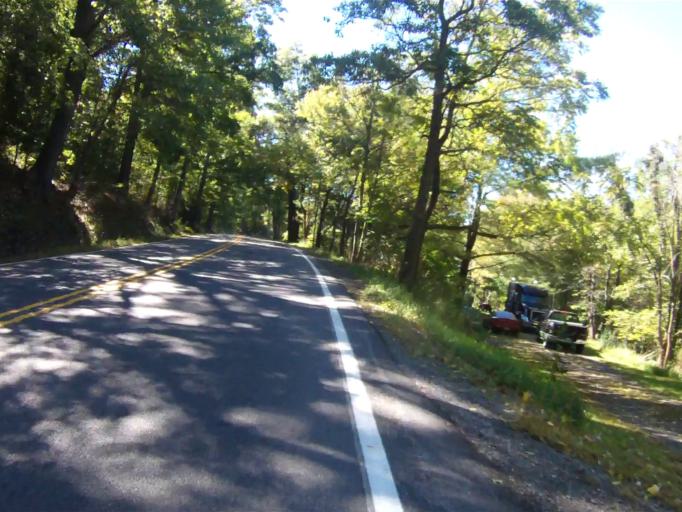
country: US
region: Pennsylvania
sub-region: Centre County
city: Park Forest Village
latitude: 40.9297
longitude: -77.9185
